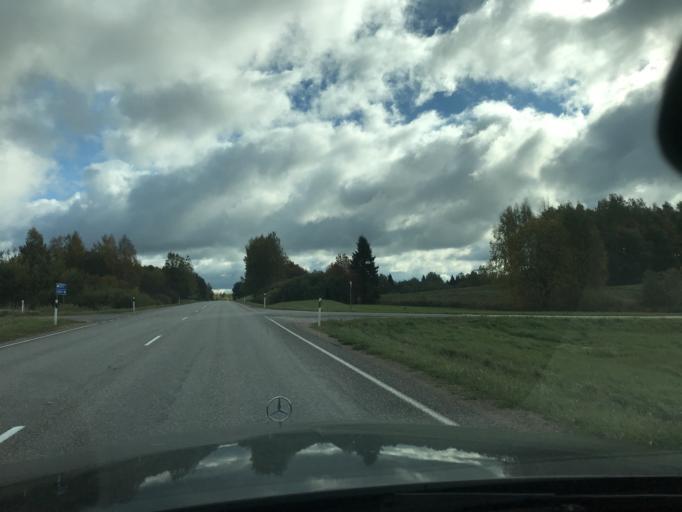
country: EE
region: Vorumaa
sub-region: Voru linn
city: Voru
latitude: 57.7587
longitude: 27.2114
